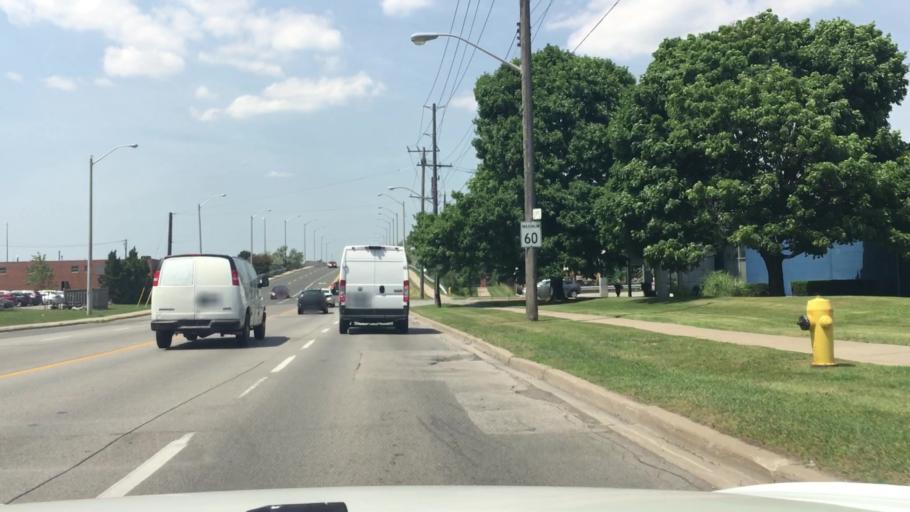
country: CA
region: Ontario
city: Scarborough
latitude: 43.7682
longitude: -79.2924
